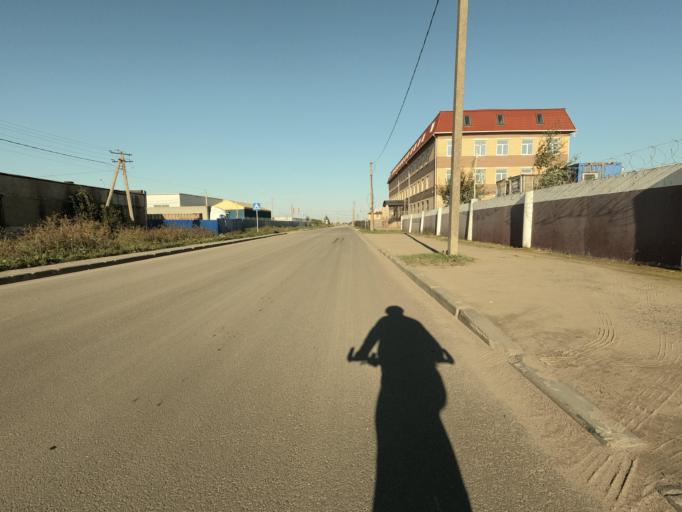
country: RU
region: St.-Petersburg
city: Petro-Slavyanka
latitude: 59.7636
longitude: 30.4834
